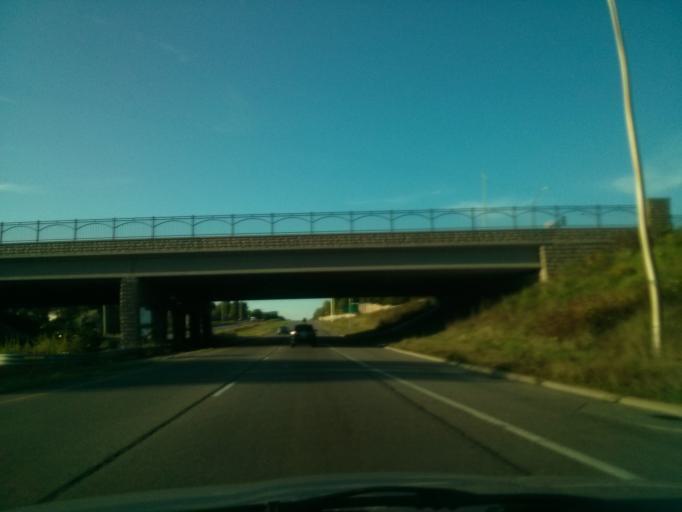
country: US
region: Minnesota
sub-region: Scott County
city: Savage
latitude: 44.8181
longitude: -93.3980
